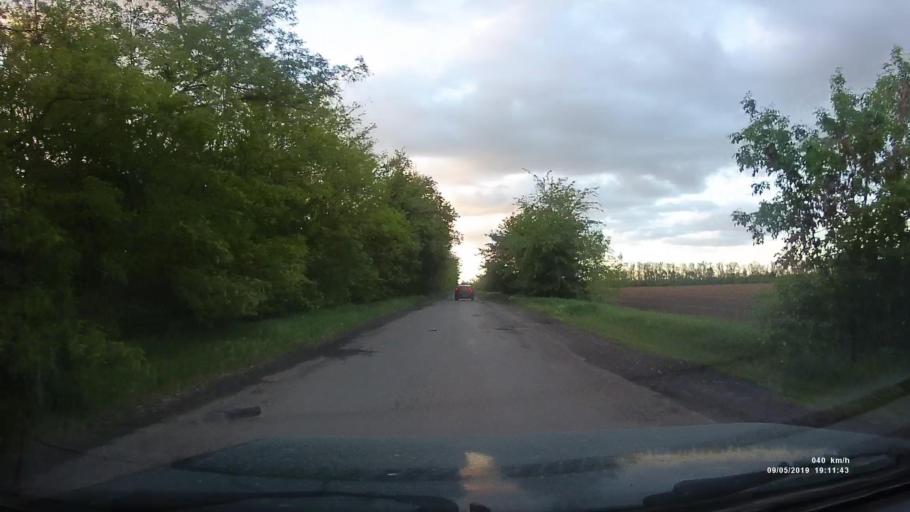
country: RU
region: Krasnodarskiy
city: Kanelovskaya
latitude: 46.7370
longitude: 39.2136
